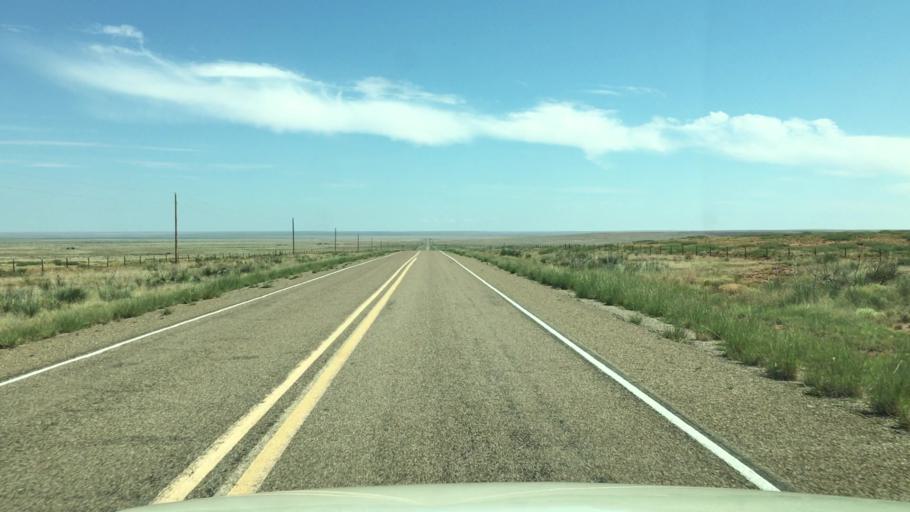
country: US
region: New Mexico
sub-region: Chaves County
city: Roswell
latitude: 33.9763
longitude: -104.5768
